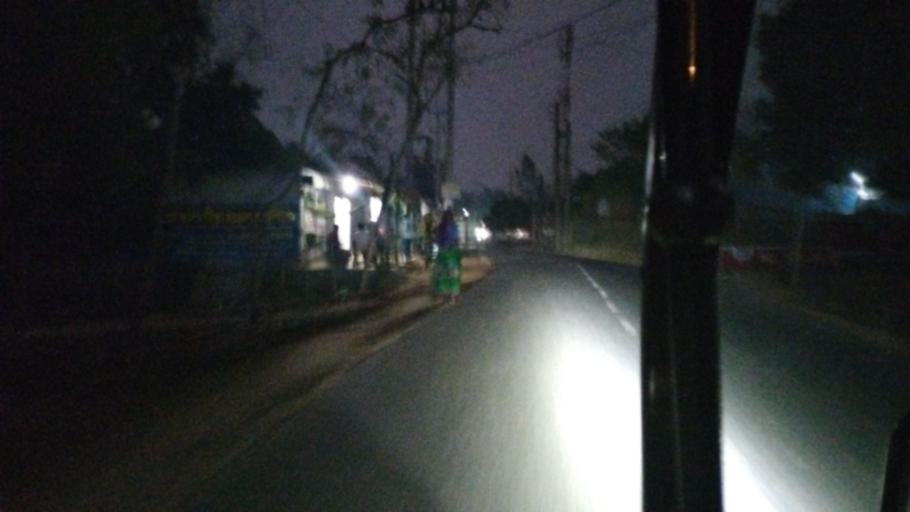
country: BD
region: Dhaka
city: Gafargaon
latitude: 24.4020
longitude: 90.3567
